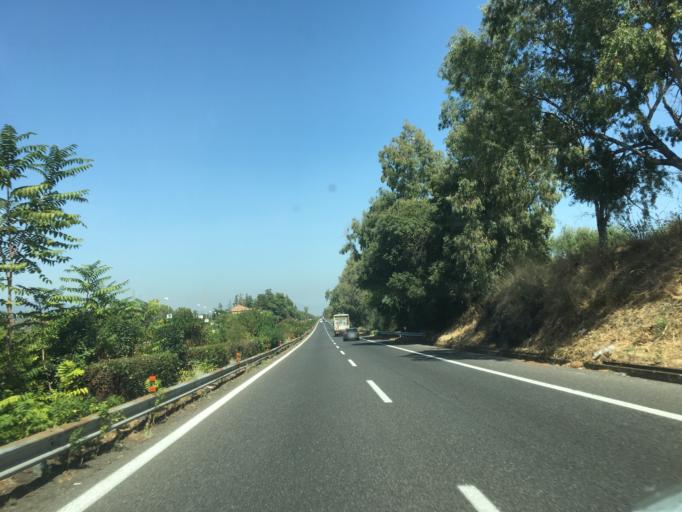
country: IT
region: Sicily
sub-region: Catania
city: Acireale
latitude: 37.6400
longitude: 15.1454
